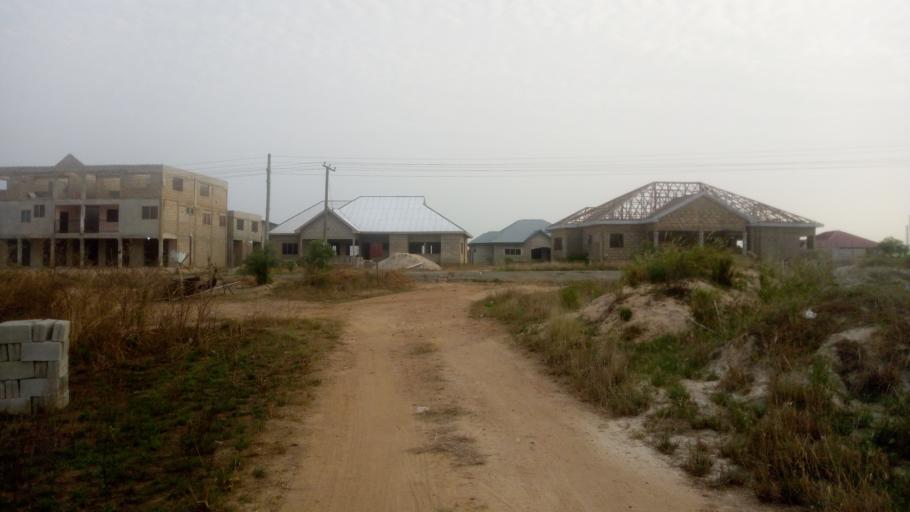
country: GH
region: Central
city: Winneba
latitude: 5.3828
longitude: -0.6286
